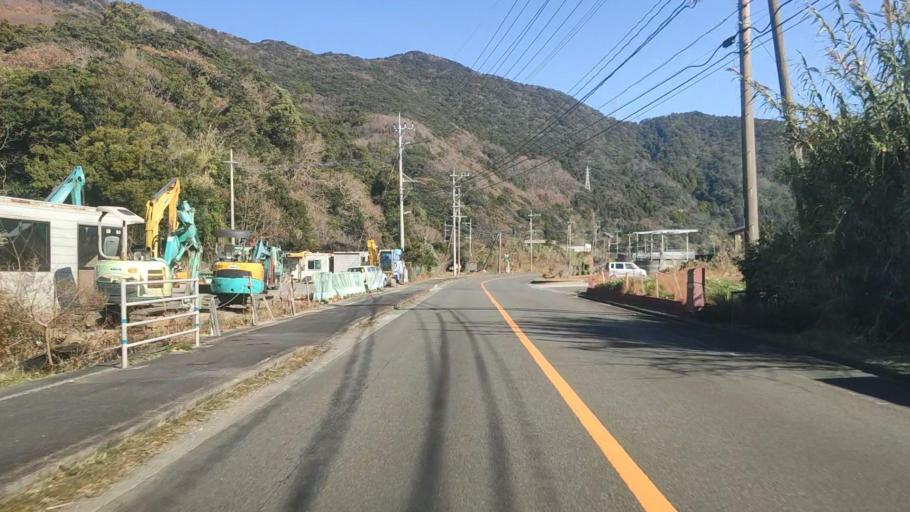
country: JP
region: Oita
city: Saiki
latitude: 32.8060
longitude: 131.9460
